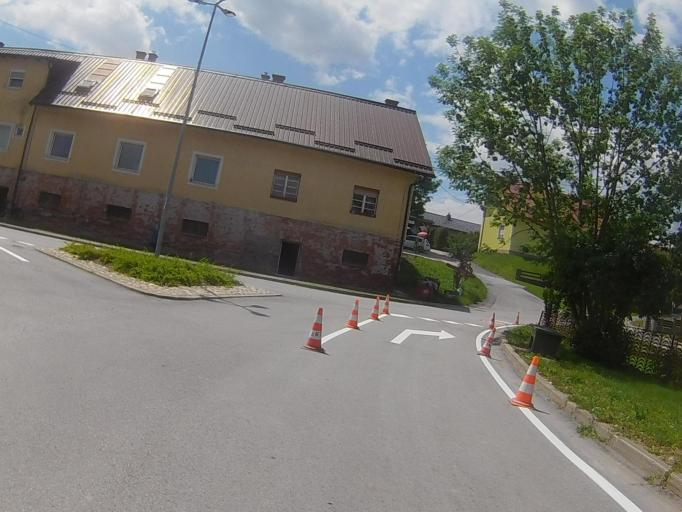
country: SI
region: Kidricevo
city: Kidricevo
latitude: 46.4417
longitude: 15.8122
